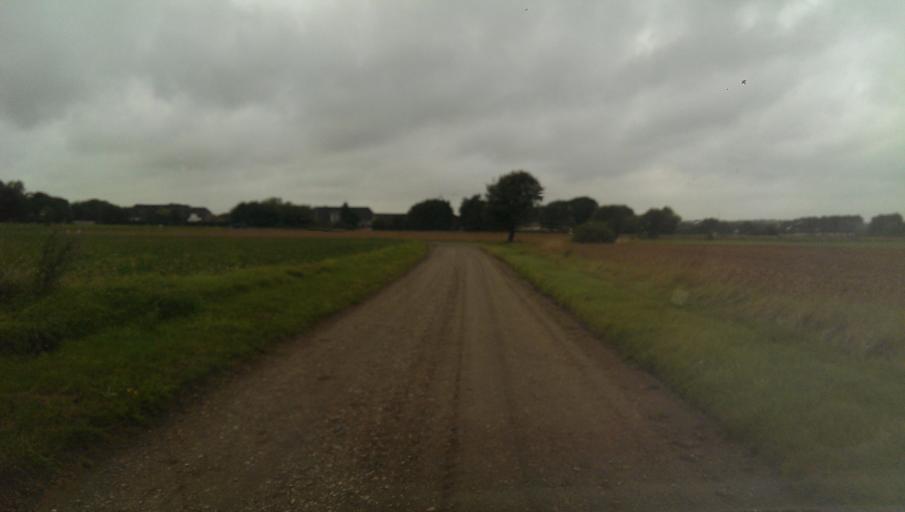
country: DK
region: South Denmark
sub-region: Esbjerg Kommune
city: Tjaereborg
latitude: 55.4884
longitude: 8.5975
